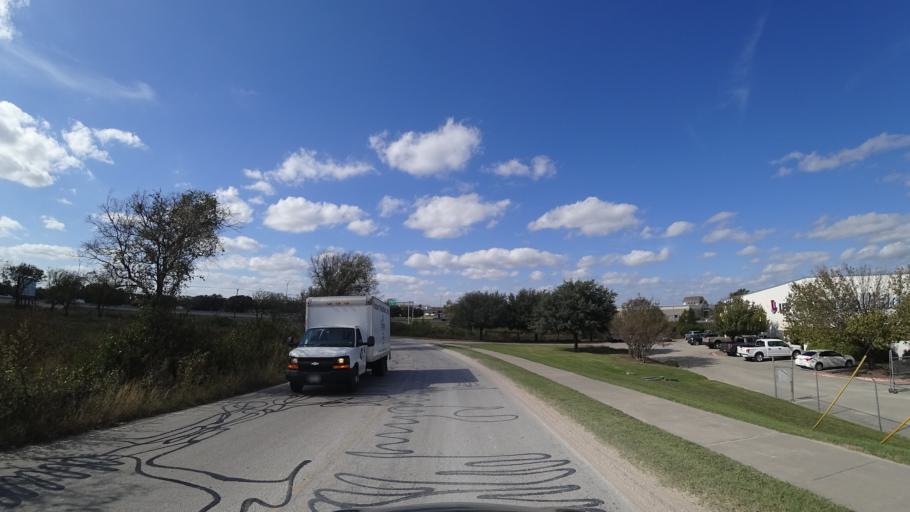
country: US
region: Texas
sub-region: Travis County
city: Windemere
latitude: 30.4696
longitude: -97.6687
